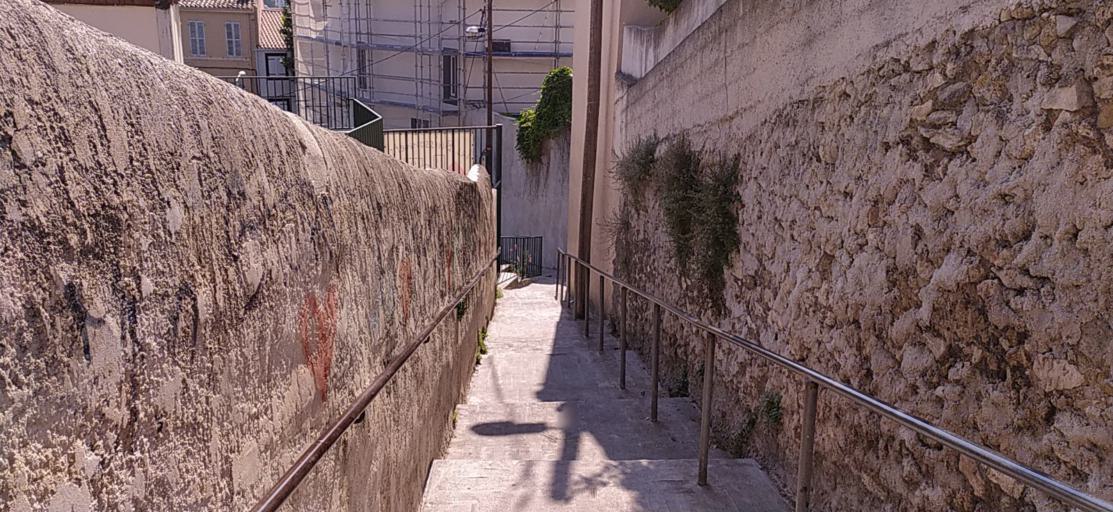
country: FR
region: Provence-Alpes-Cote d'Azur
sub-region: Departement des Bouches-du-Rhone
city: Marseille 14
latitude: 43.3458
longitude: 5.3587
